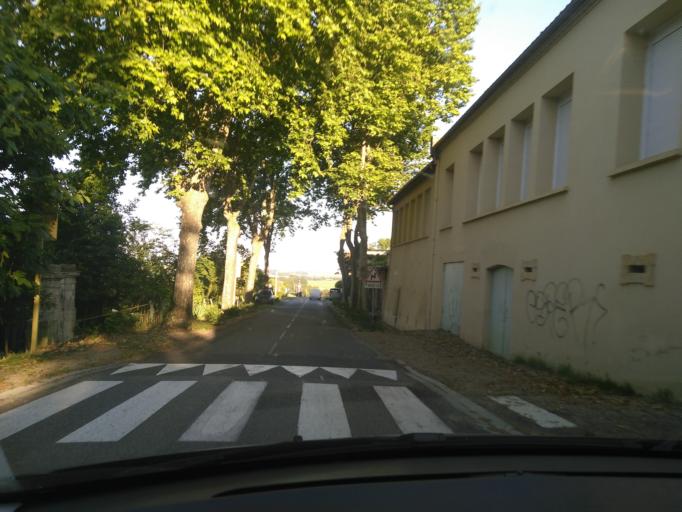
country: FR
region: Midi-Pyrenees
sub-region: Departement du Gers
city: Valence-sur-Baise
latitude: 43.8756
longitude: 0.4618
